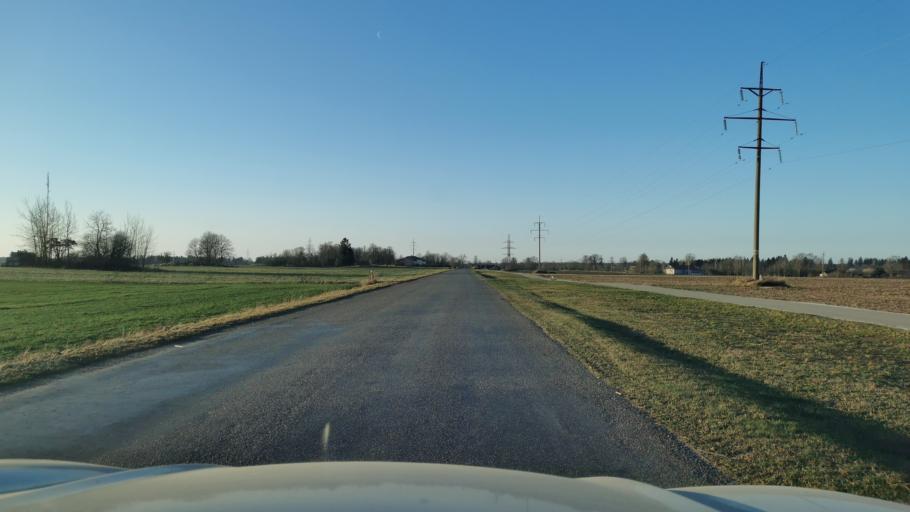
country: EE
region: Ida-Virumaa
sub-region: Puessi linn
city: Pussi
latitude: 59.3406
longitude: 27.0284
